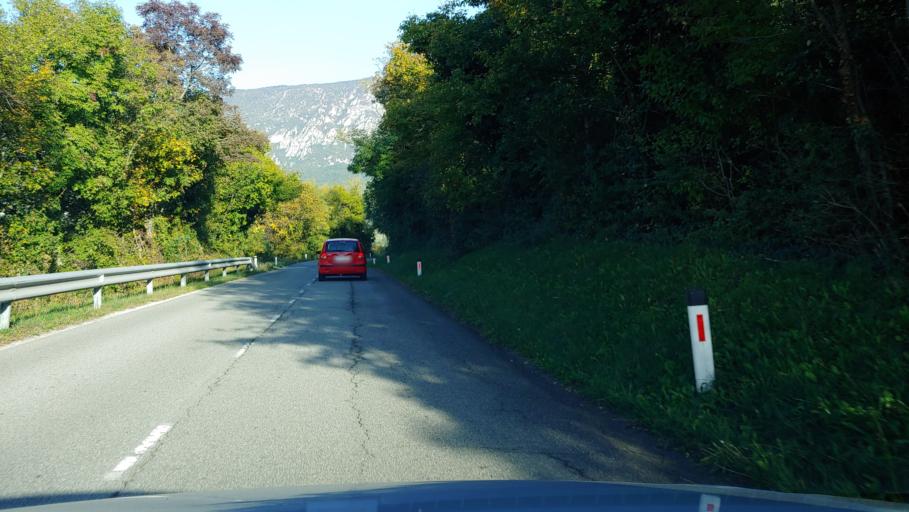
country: SI
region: Vipava
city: Vipava
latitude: 45.8178
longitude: 13.9354
